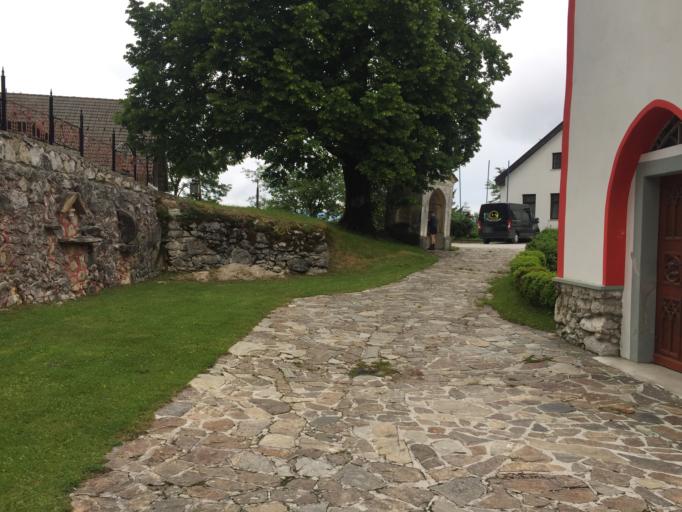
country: SI
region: Dobrna
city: Dobrna
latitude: 46.3871
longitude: 15.1926
